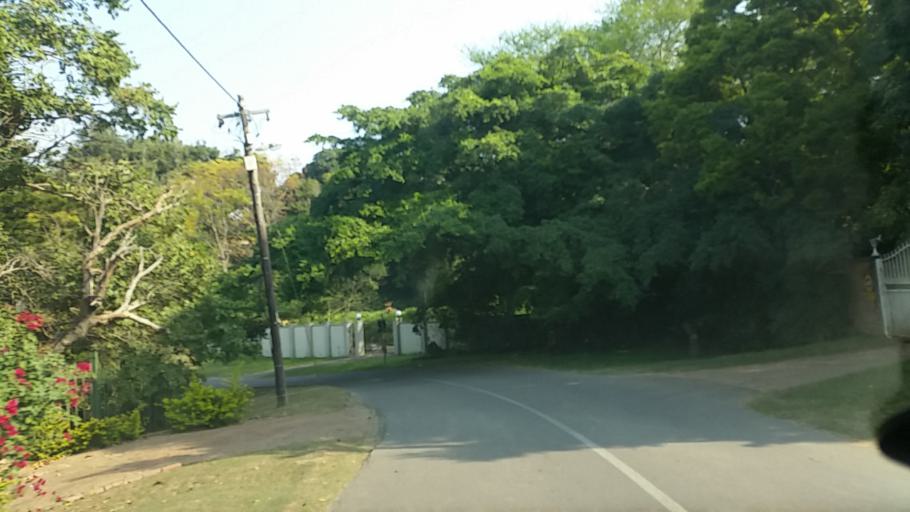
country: ZA
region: KwaZulu-Natal
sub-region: eThekwini Metropolitan Municipality
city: Berea
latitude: -29.8391
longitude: 30.9470
